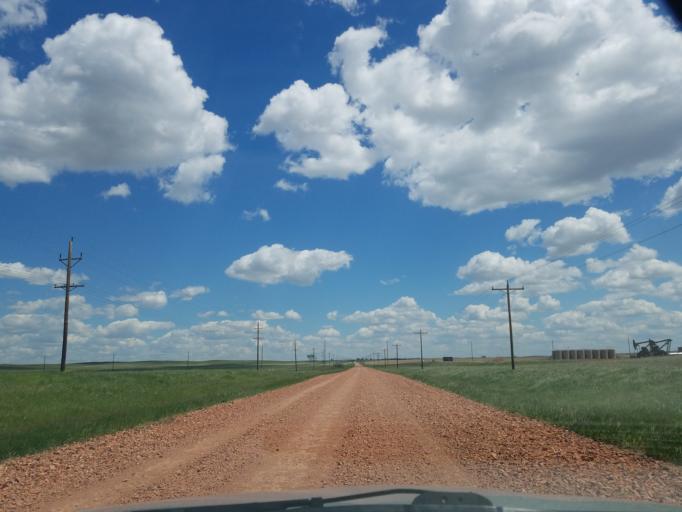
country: US
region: North Dakota
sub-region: McKenzie County
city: Watford City
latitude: 47.8194
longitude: -103.5915
